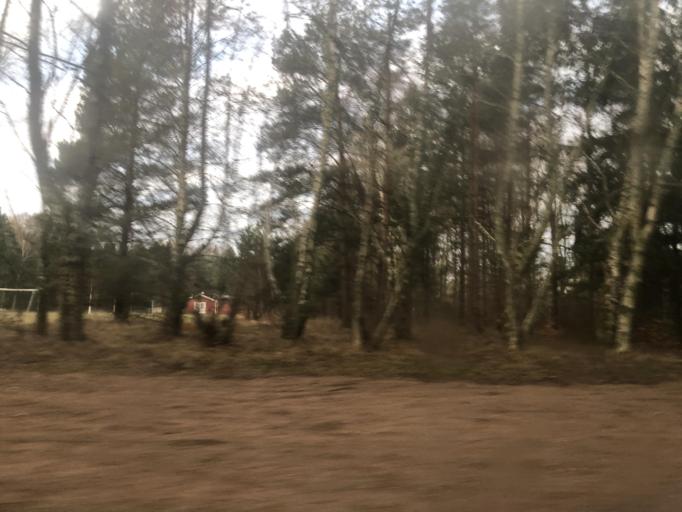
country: SE
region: Skane
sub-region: Sjobo Kommun
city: Blentarp
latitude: 55.6171
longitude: 13.5479
